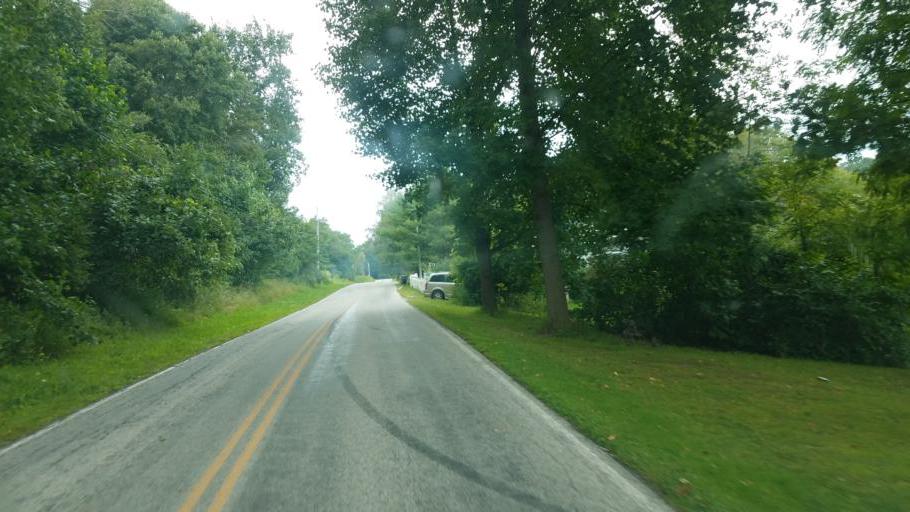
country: US
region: Ohio
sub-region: Sandusky County
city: Bellville
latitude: 40.6266
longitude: -82.4197
